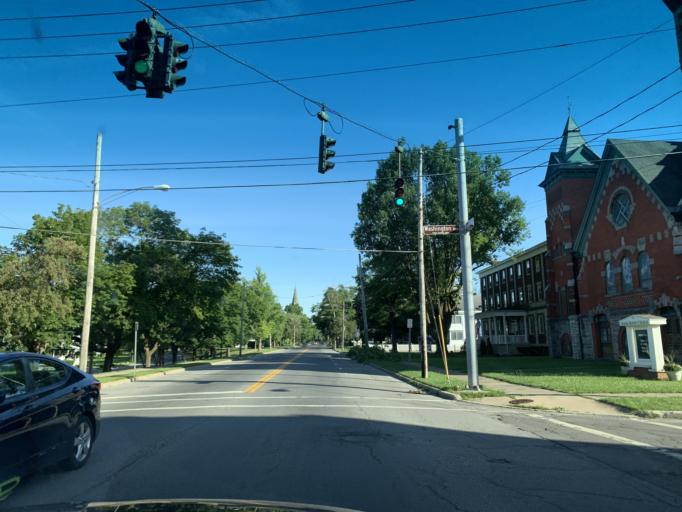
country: US
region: New York
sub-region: Madison County
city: Oneida
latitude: 43.0930
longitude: -75.6507
